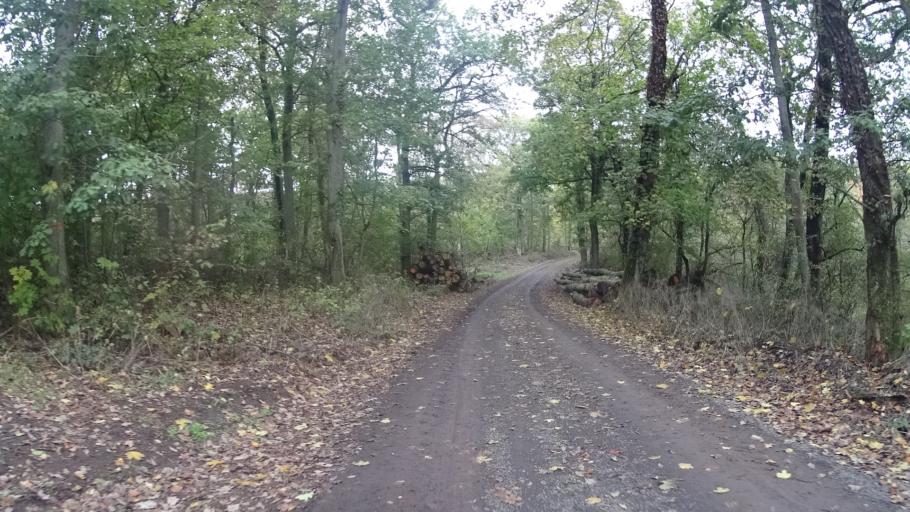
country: DE
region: Rheinland-Pfalz
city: Dannenfels
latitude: 49.6563
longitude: 7.9513
